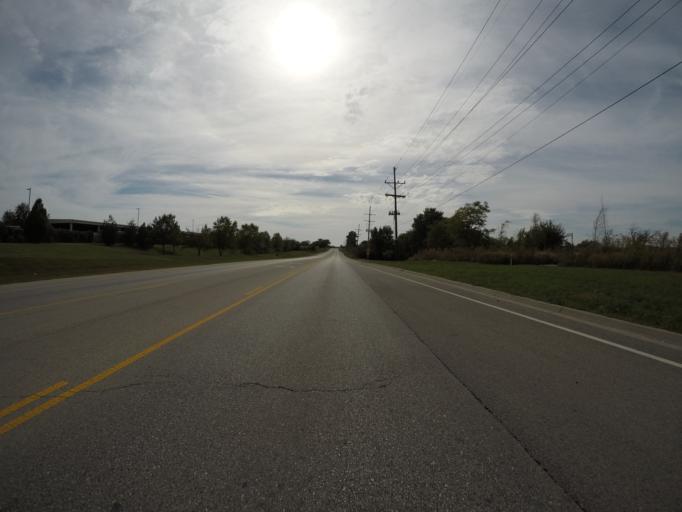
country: US
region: Kansas
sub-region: Johnson County
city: Olathe
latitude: 38.8643
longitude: -94.8458
